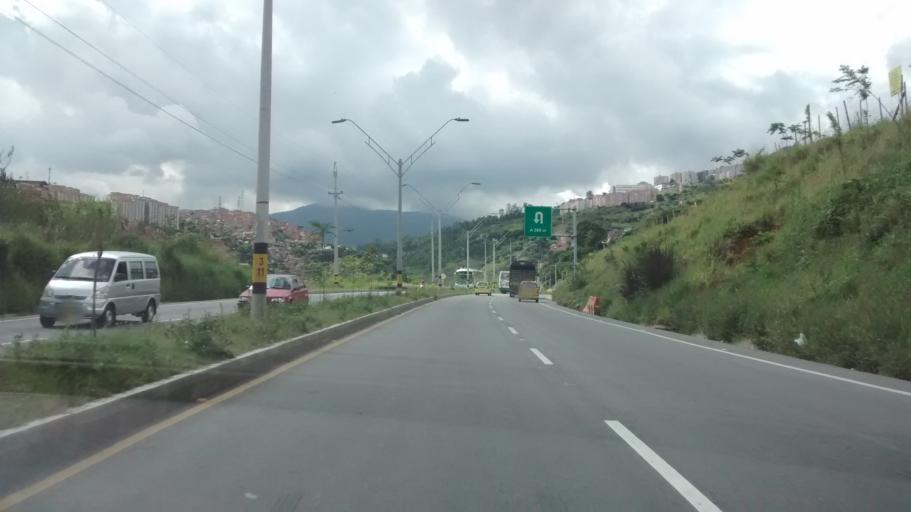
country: CO
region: Antioquia
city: Medellin
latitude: 6.2753
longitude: -75.6001
